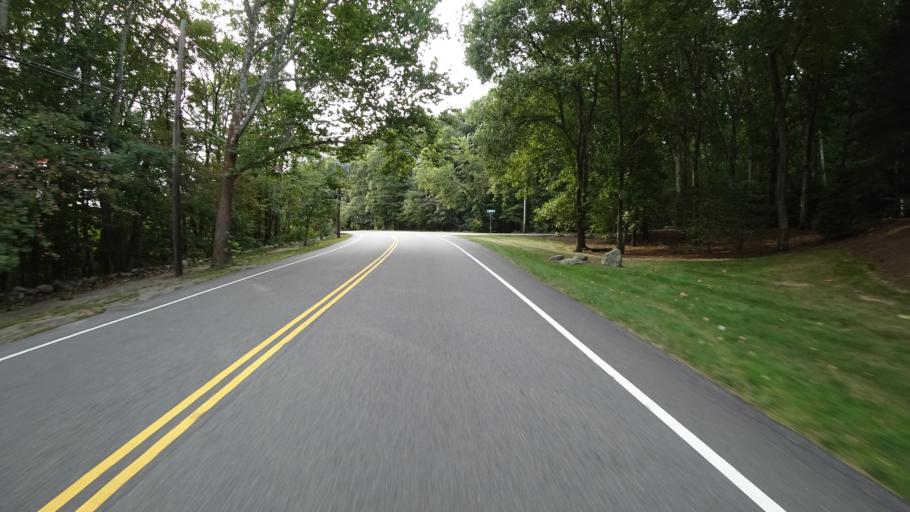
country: US
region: Massachusetts
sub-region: Norfolk County
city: Needham
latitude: 42.2546
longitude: -71.2295
